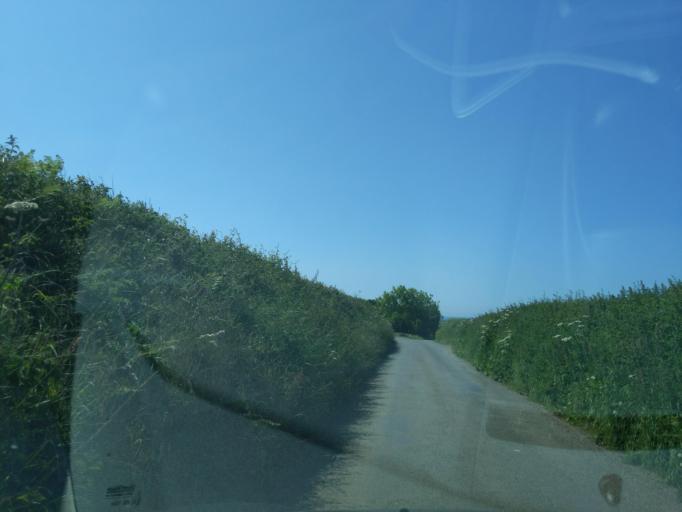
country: GB
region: England
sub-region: Cornwall
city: Wadebridge
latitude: 50.5822
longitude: -4.8392
